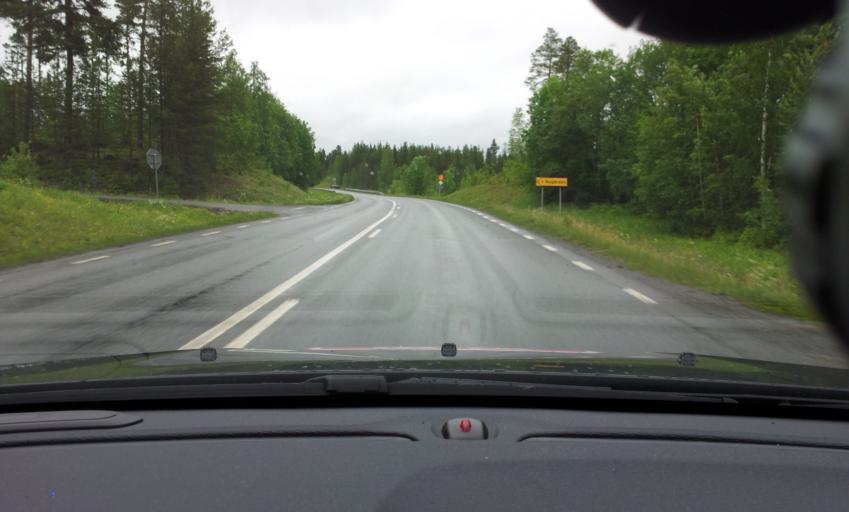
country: SE
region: Jaemtland
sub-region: Krokoms Kommun
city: Krokom
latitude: 63.3402
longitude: 14.4663
